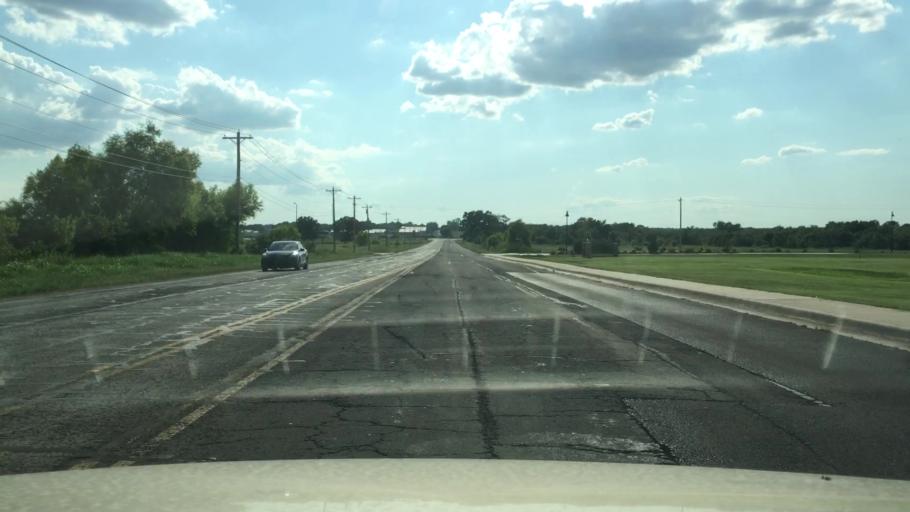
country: US
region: Oklahoma
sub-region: Cherokee County
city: Tahlequah
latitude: 35.9299
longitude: -94.9919
